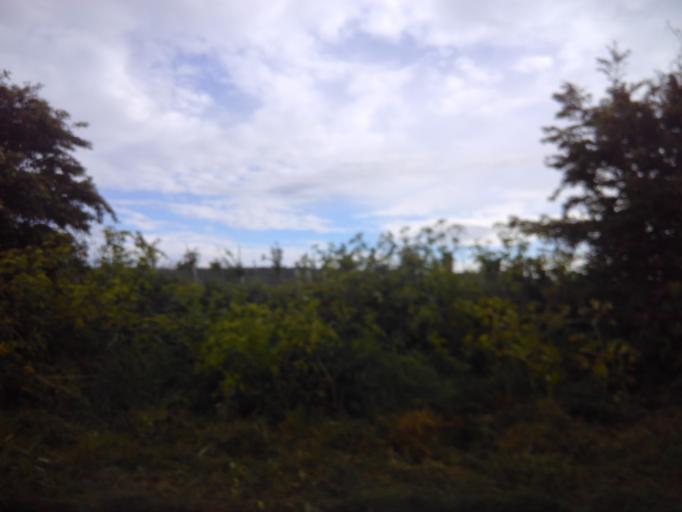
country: GB
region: England
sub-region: Norfolk
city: Sheringham
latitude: 52.9428
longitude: 1.1503
